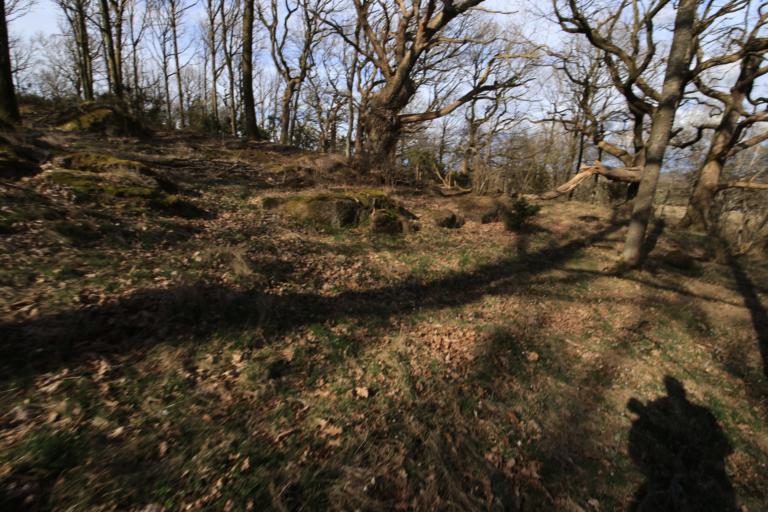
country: SE
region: Halland
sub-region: Varbergs Kommun
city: Varberg
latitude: 57.1751
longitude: 12.2730
